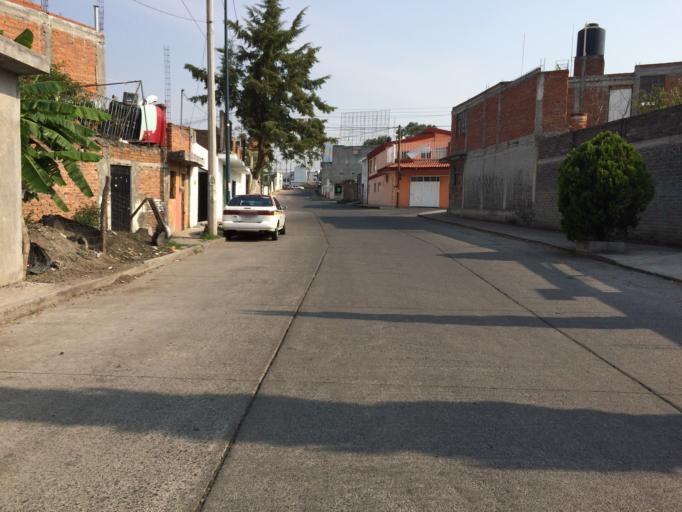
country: MX
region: Michoacan
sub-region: Tarimbaro
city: Real Hacienda (Metropolis)
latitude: 19.7251
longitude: -101.2139
